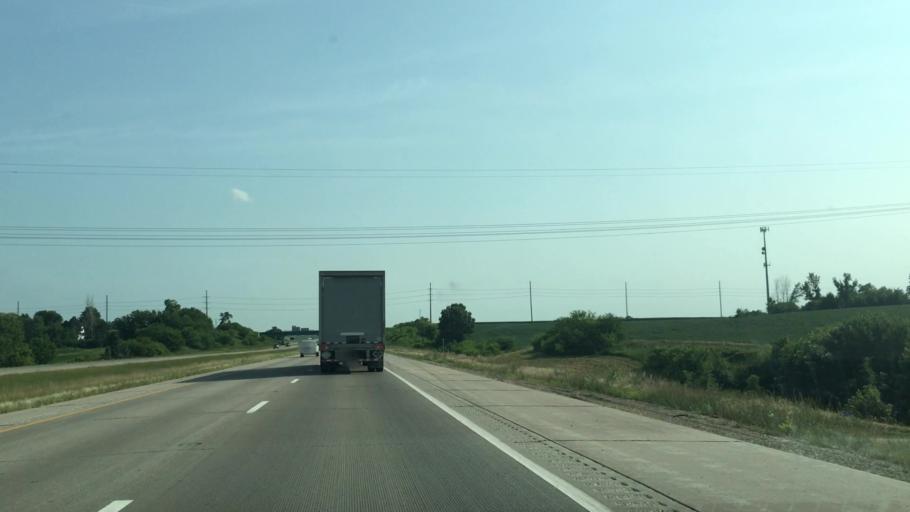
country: US
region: Iowa
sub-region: Scott County
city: Walcott
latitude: 41.5754
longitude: -90.6777
